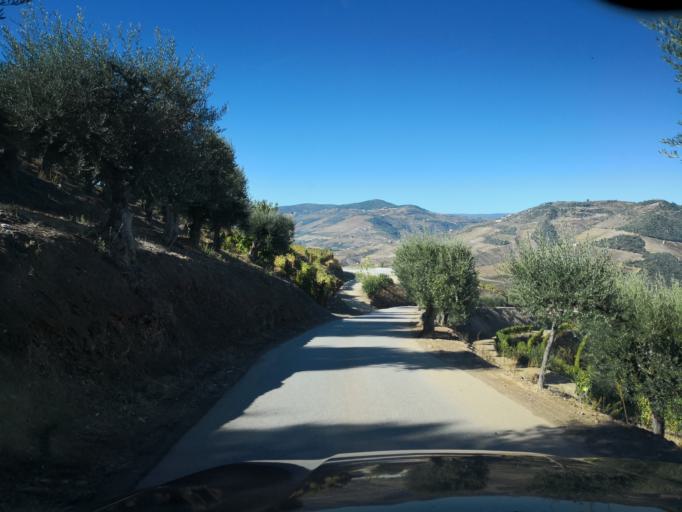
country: PT
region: Viseu
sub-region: Tabuaco
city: Tabuaco
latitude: 41.1725
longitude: -7.5143
